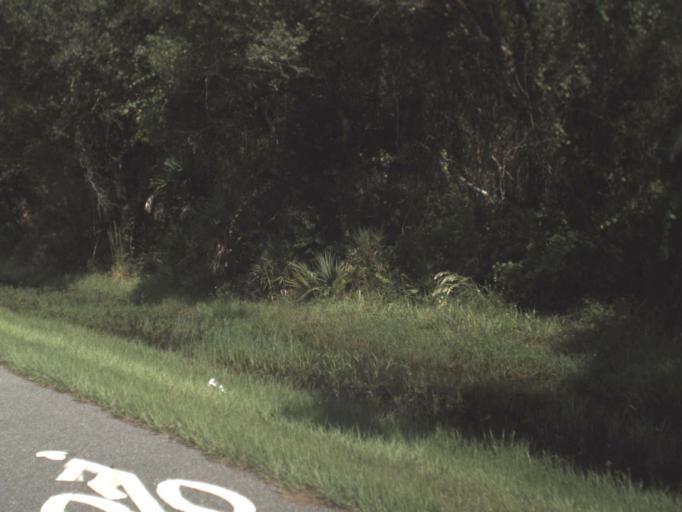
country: US
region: Florida
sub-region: Sarasota County
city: Lake Sarasota
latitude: 27.2541
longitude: -82.3947
